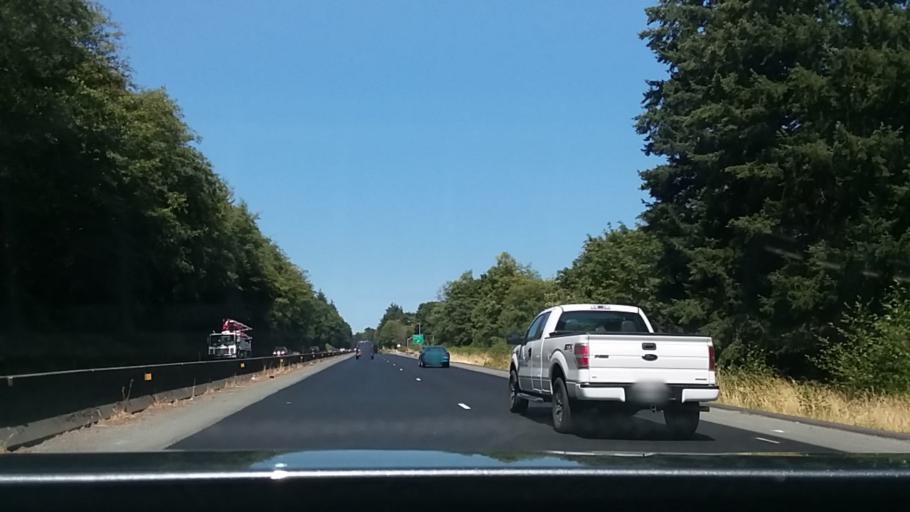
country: US
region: Washington
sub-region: Skagit County
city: Anacortes
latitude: 48.4849
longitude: -122.5972
